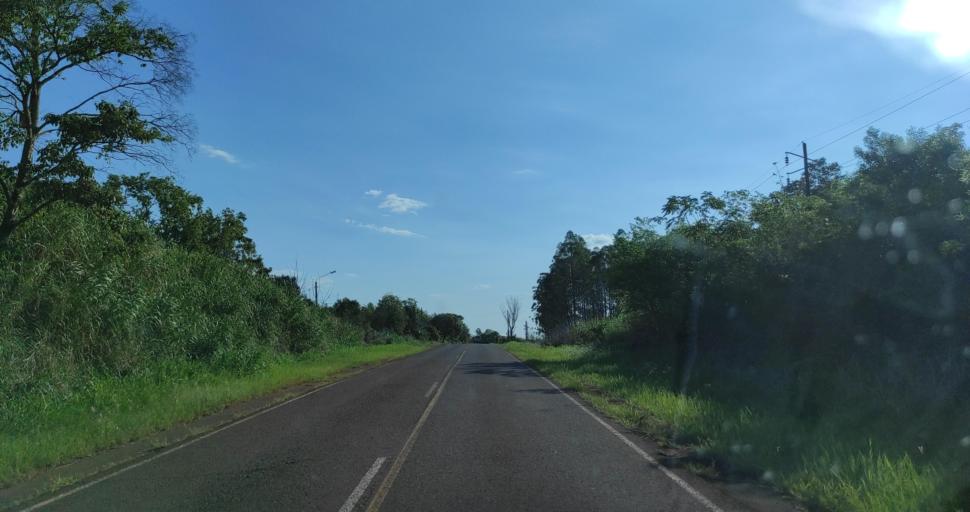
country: AR
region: Misiones
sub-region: Departamento de Eldorado
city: Eldorado
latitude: -26.3822
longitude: -54.3416
